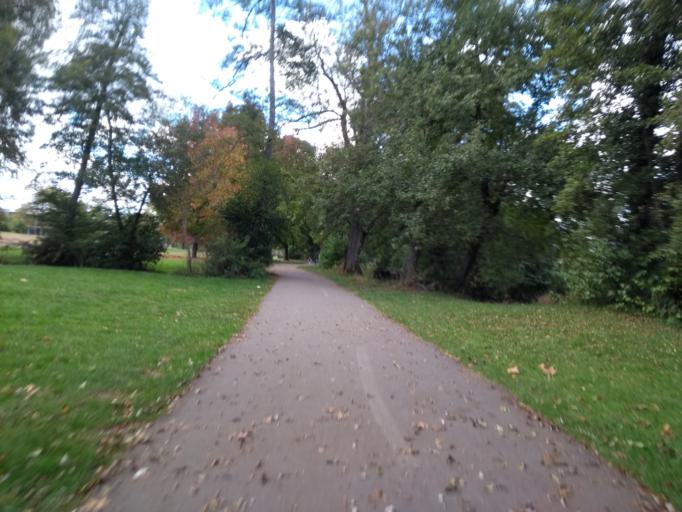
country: FR
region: Aquitaine
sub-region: Departement de la Gironde
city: Gradignan
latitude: 44.7684
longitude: -0.6079
